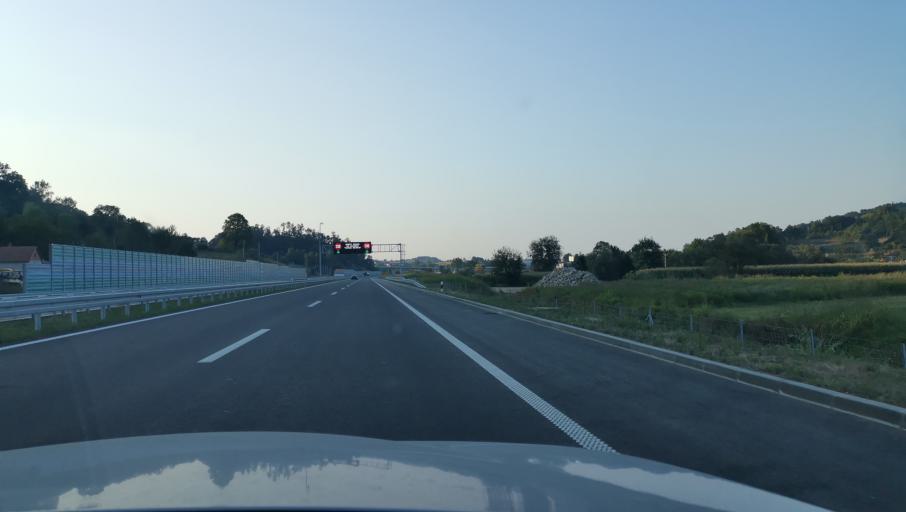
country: RS
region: Central Serbia
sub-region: Kolubarski Okrug
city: Ljig
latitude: 44.2232
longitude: 20.2553
